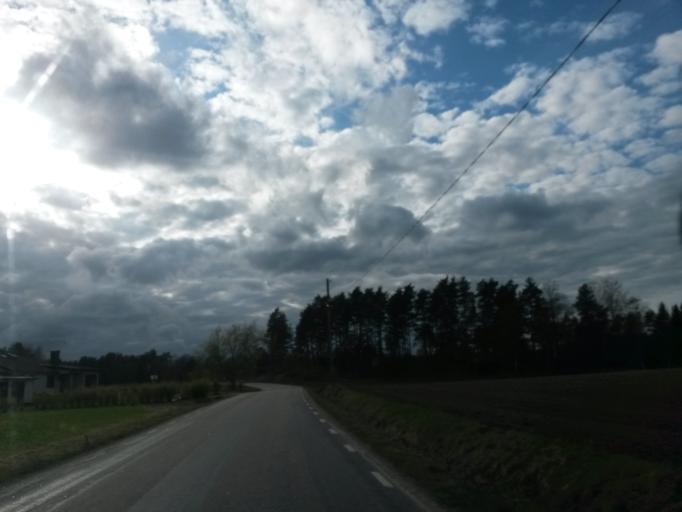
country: SE
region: Vaestra Goetaland
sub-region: Vargarda Kommun
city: Jonstorp
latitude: 58.0134
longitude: 12.6572
